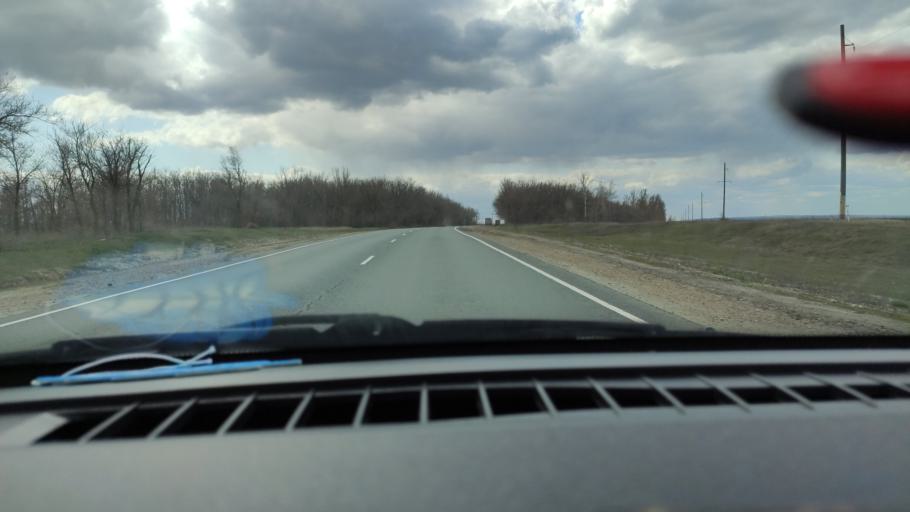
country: RU
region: Saratov
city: Alekseyevka
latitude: 52.2692
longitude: 47.9277
